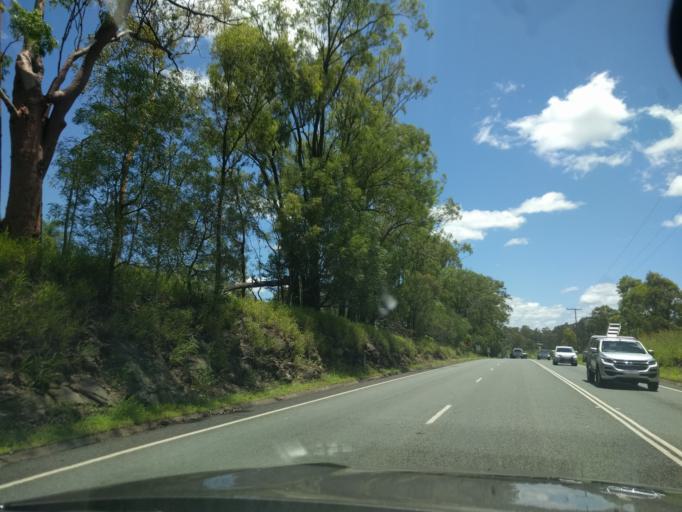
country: AU
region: Queensland
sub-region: Logan
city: Cedar Vale
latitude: -27.8401
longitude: 153.0245
